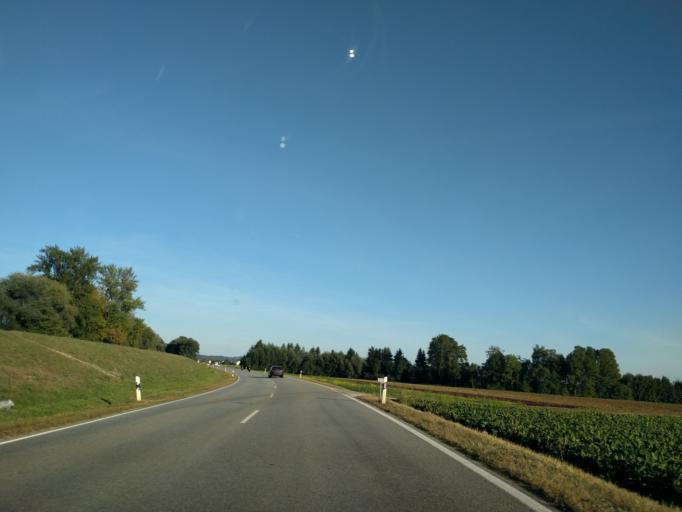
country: DE
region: Bavaria
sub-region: Lower Bavaria
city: Osterhofen
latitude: 48.7159
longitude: 13.0212
